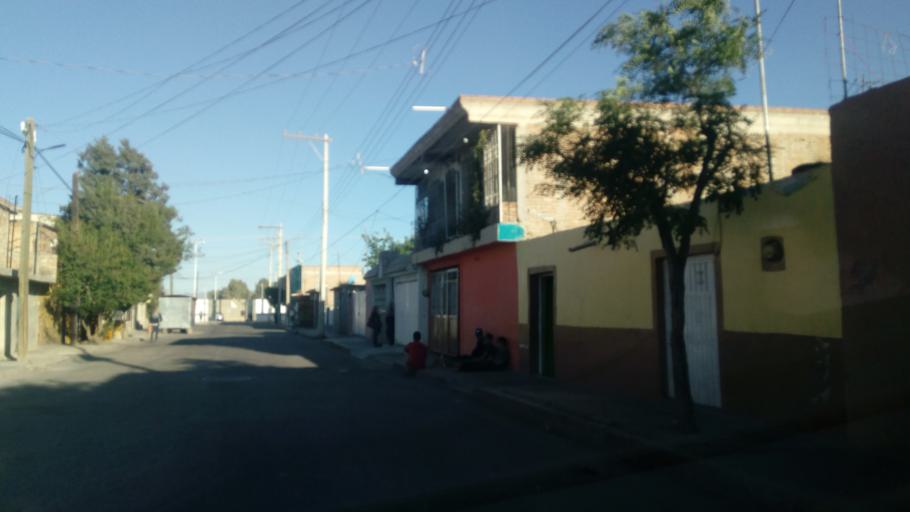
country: MX
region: Durango
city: Victoria de Durango
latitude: 23.9973
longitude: -104.6803
